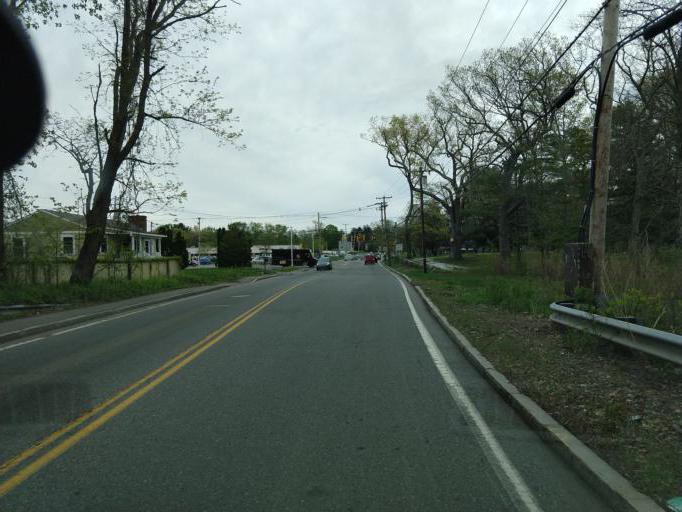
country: US
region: Massachusetts
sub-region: Middlesex County
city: Tewksbury
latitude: 42.5888
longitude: -71.2038
